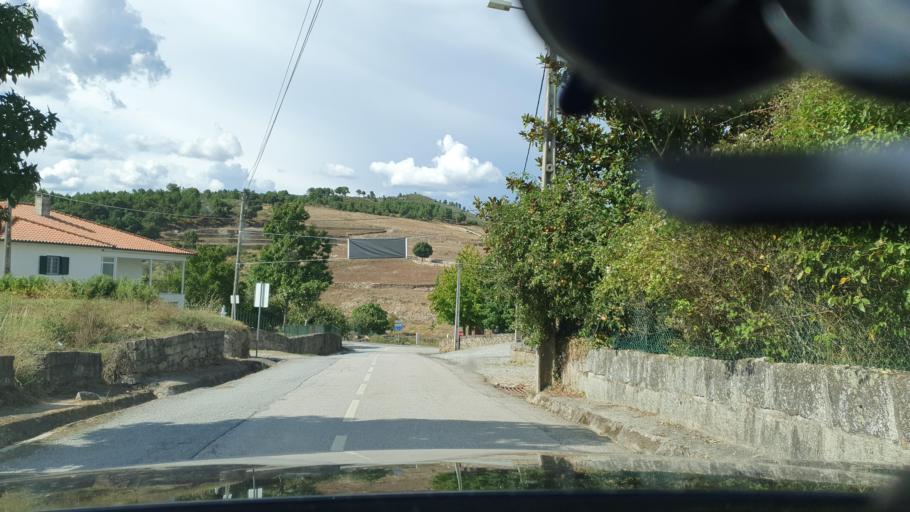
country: PT
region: Vila Real
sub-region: Boticas
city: Boticas
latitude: 41.7086
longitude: -7.5680
